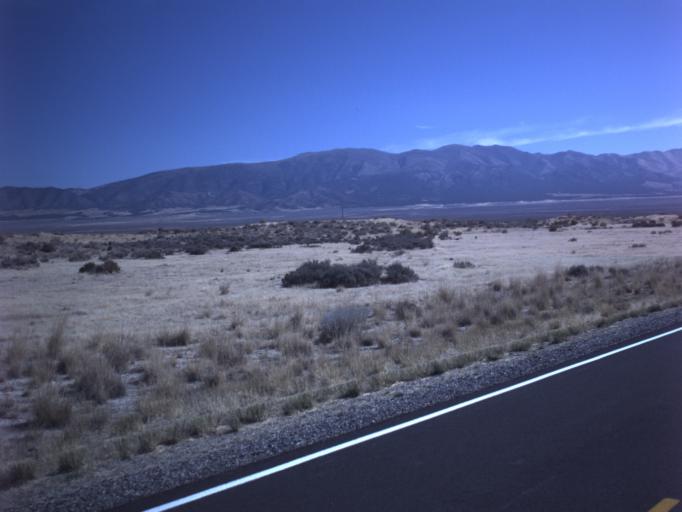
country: US
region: Utah
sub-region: Tooele County
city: Grantsville
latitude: 40.2514
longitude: -112.7338
